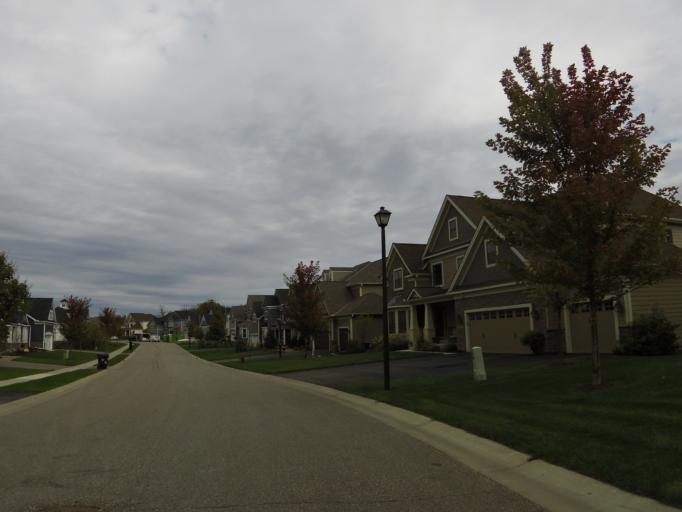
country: US
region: Minnesota
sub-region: Hennepin County
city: Eden Prairie
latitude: 44.8219
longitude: -93.4844
